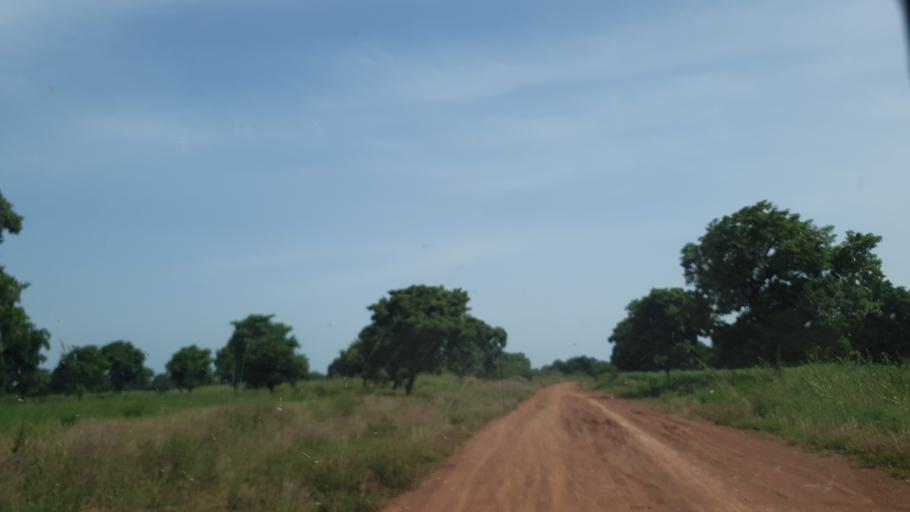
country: ML
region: Koulikoro
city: Dioila
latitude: 12.4145
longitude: -6.2374
